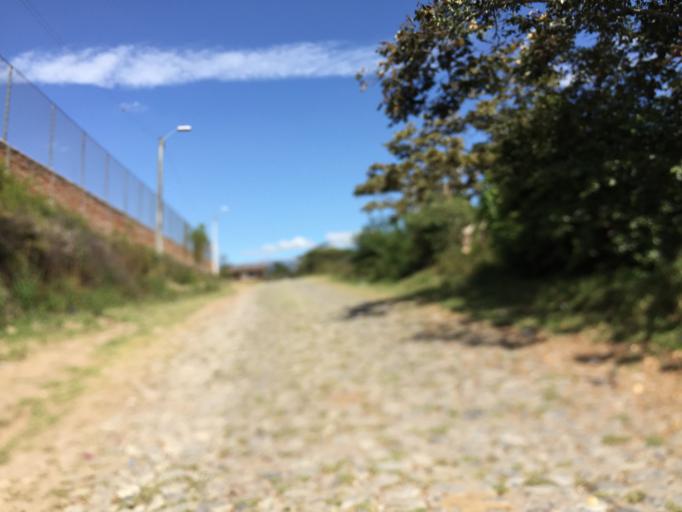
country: EC
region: Imbabura
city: Ibarra
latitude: 0.3172
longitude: -78.1592
